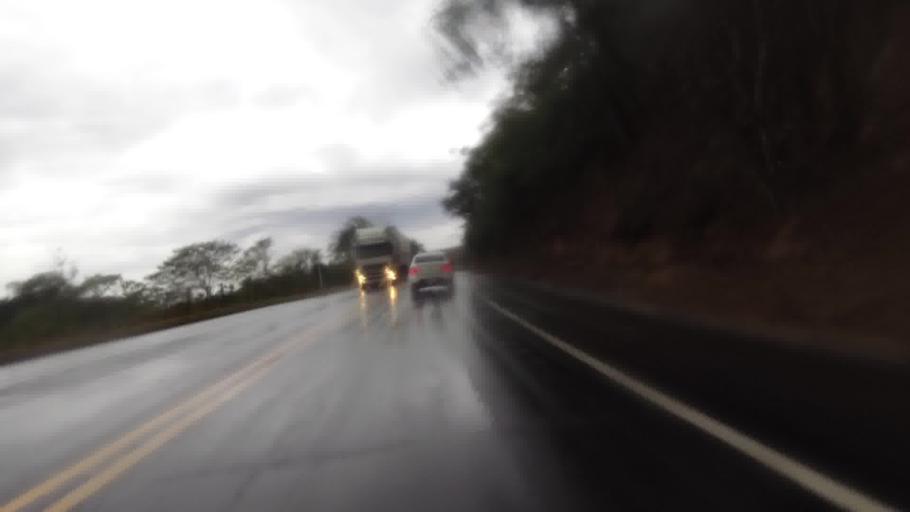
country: BR
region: Espirito Santo
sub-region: Cachoeiro De Itapemirim
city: Cachoeiro de Itapemirim
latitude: -20.9860
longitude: -41.1184
